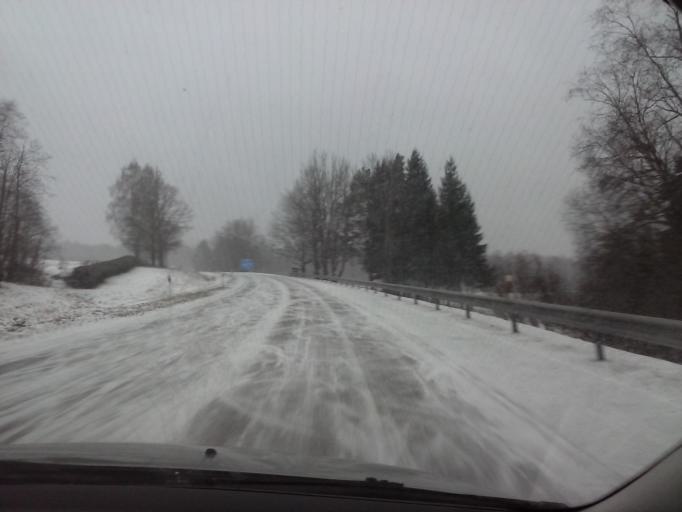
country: EE
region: Valgamaa
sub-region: Torva linn
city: Torva
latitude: 58.0177
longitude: 26.1625
